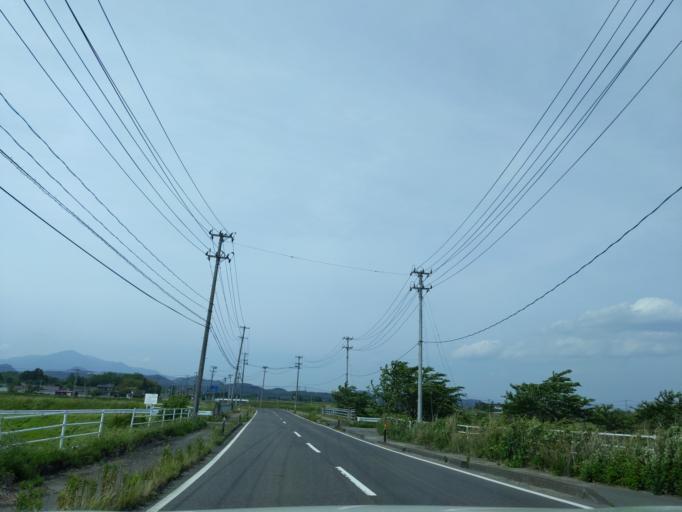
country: JP
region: Fukushima
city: Koriyama
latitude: 37.4527
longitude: 140.3126
